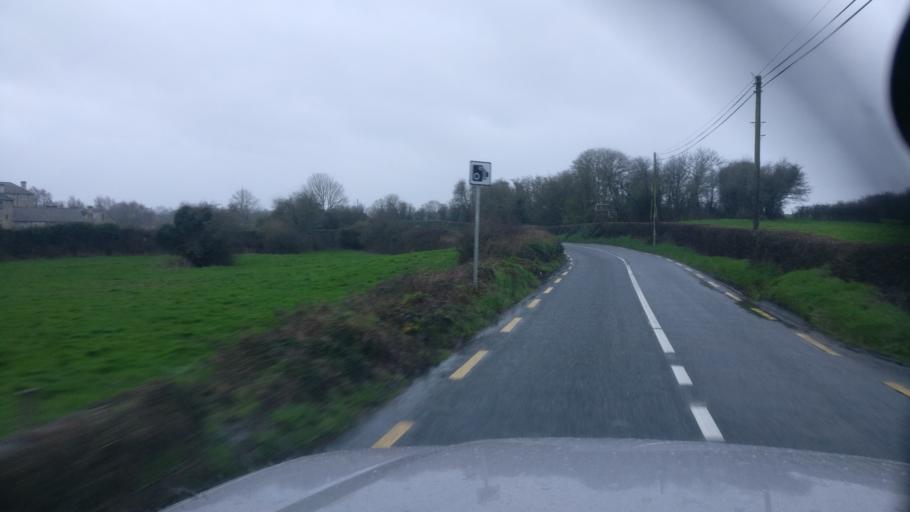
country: IE
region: Connaught
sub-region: County Galway
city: Portumna
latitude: 53.1013
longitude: -8.2240
